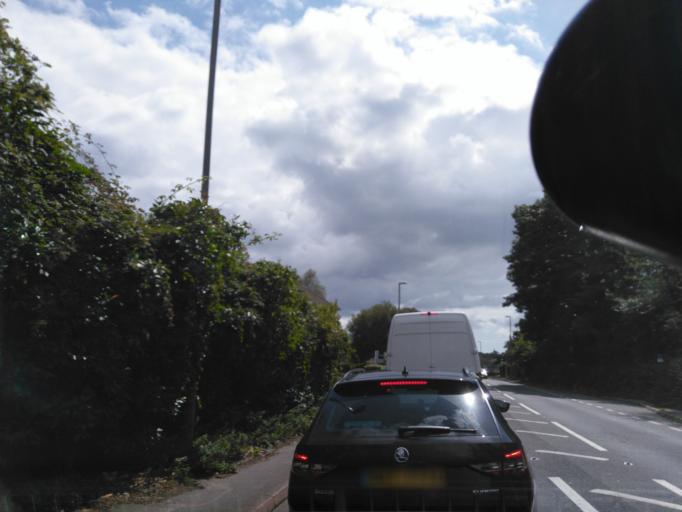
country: GB
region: England
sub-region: Dorset
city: Lytchett Matravers
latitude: 50.7524
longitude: -2.0445
